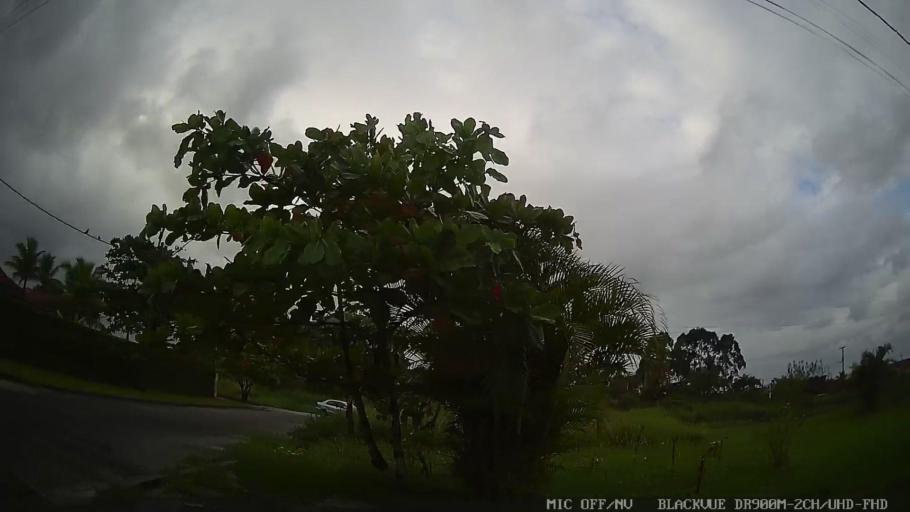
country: BR
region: Sao Paulo
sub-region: Itanhaem
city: Itanhaem
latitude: -24.2189
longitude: -46.8613
